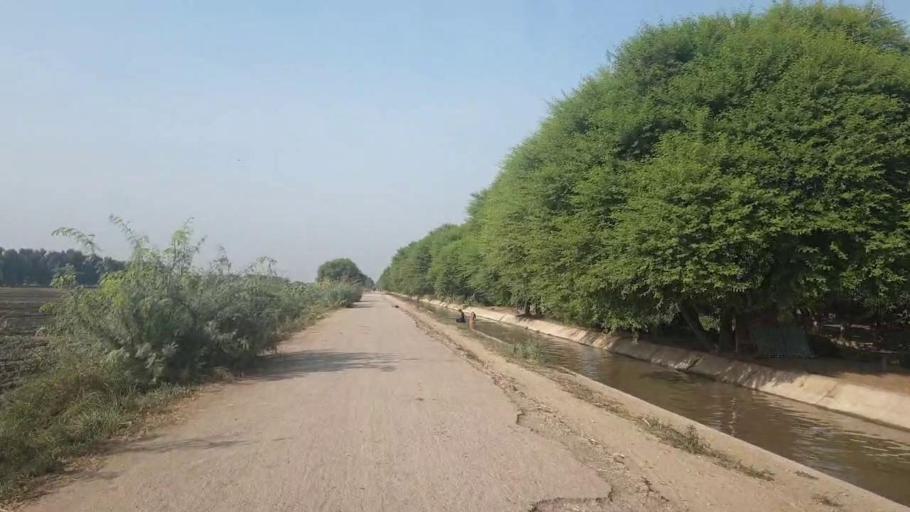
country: PK
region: Sindh
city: Tando Jam
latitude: 25.4218
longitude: 68.4622
